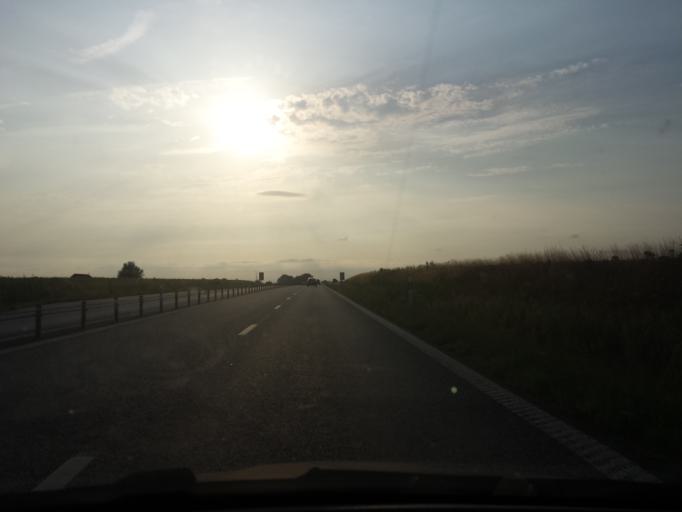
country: SE
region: Skane
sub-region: Skurups Kommun
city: Rydsgard
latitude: 55.4768
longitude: 13.6417
